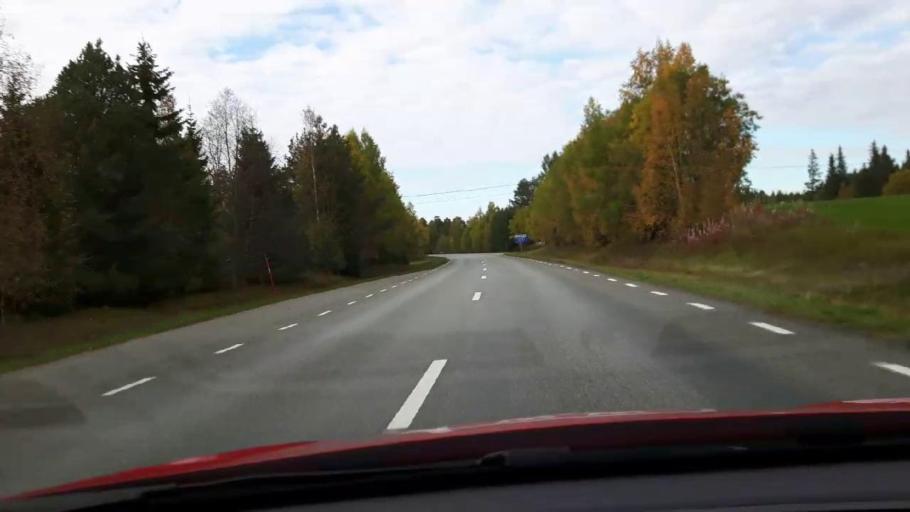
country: SE
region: Jaemtland
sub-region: Krokoms Kommun
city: Valla
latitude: 63.2539
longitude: 13.9958
